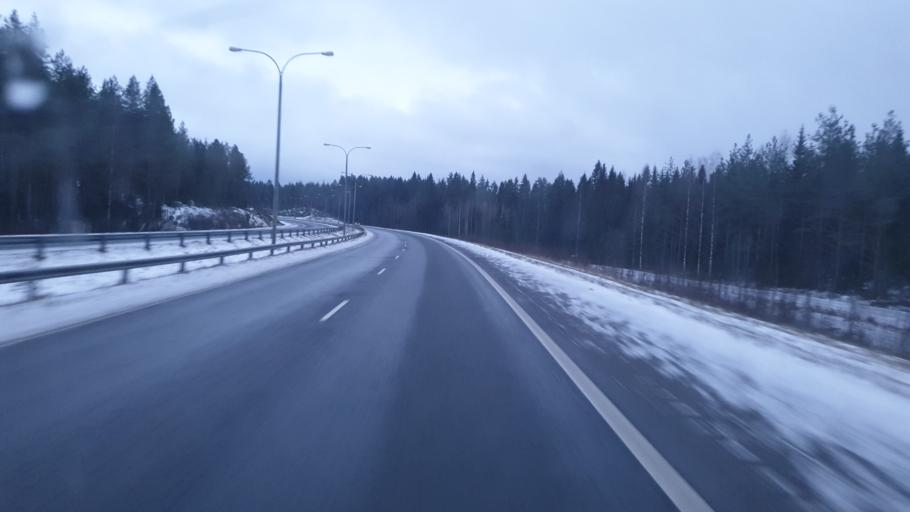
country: FI
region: Northern Savo
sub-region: Kuopio
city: Siilinjaervi
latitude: 63.0058
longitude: 27.6806
